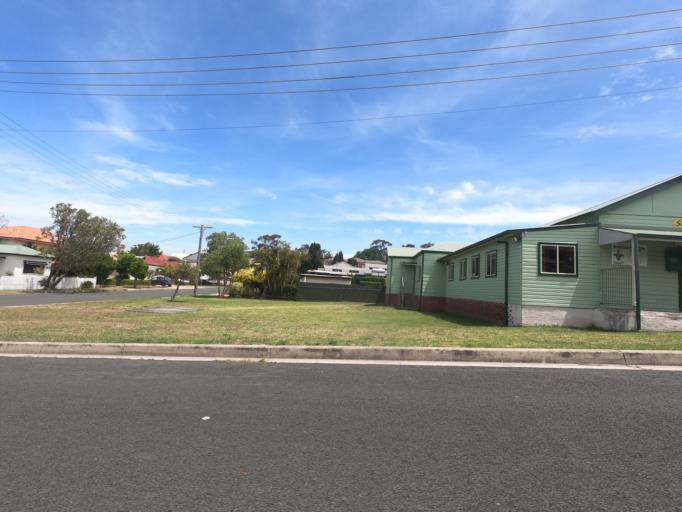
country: AU
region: New South Wales
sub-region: Wollongong
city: Mount Ousley
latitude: -34.3907
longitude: 150.8782
